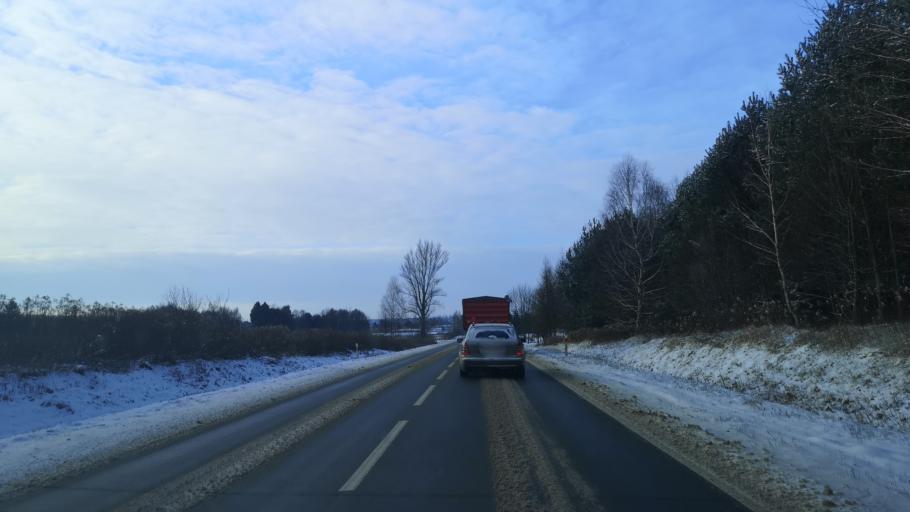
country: PL
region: Subcarpathian Voivodeship
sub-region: Powiat przeworski
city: Sieniawa
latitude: 50.2046
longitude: 22.6366
